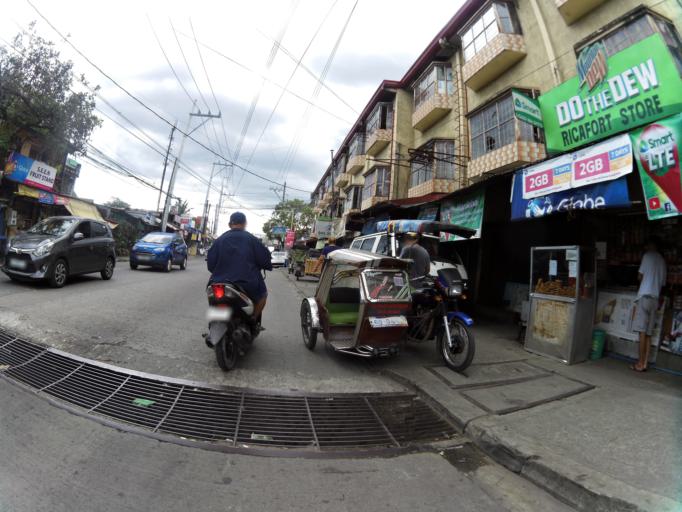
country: PH
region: Calabarzon
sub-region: Province of Rizal
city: Antipolo
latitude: 14.6362
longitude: 121.1214
